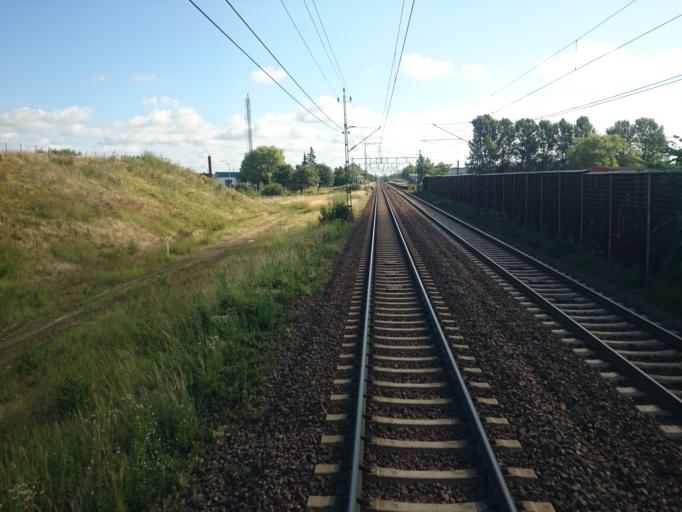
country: SE
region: Skane
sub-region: Burlovs Kommun
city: Arloev
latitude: 55.6405
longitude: 13.0794
